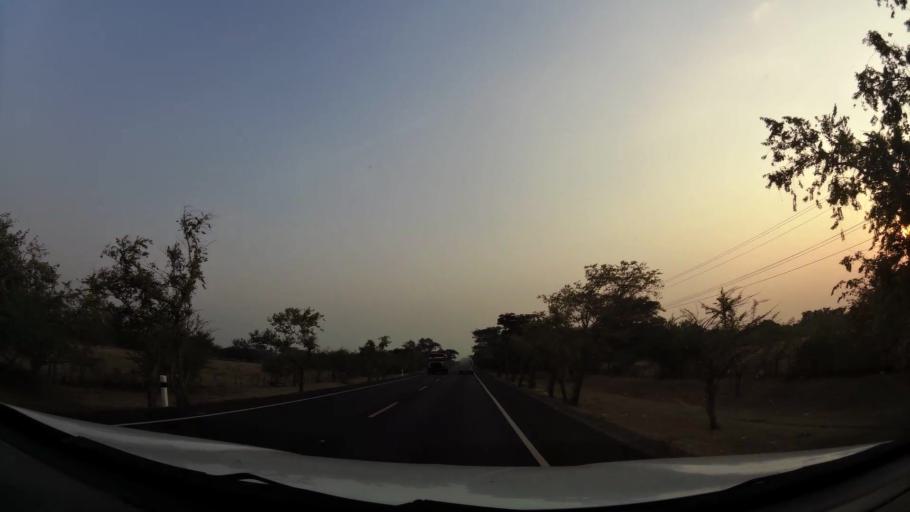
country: NI
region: Leon
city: La Paz Centro
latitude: 12.3078
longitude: -86.7045
